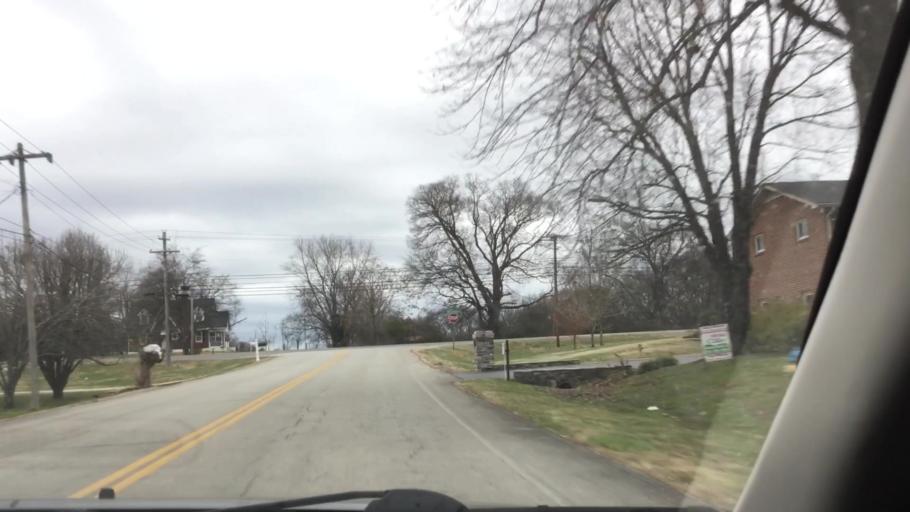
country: US
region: Tennessee
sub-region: Maury County
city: Columbia
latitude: 35.6242
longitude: -87.0964
